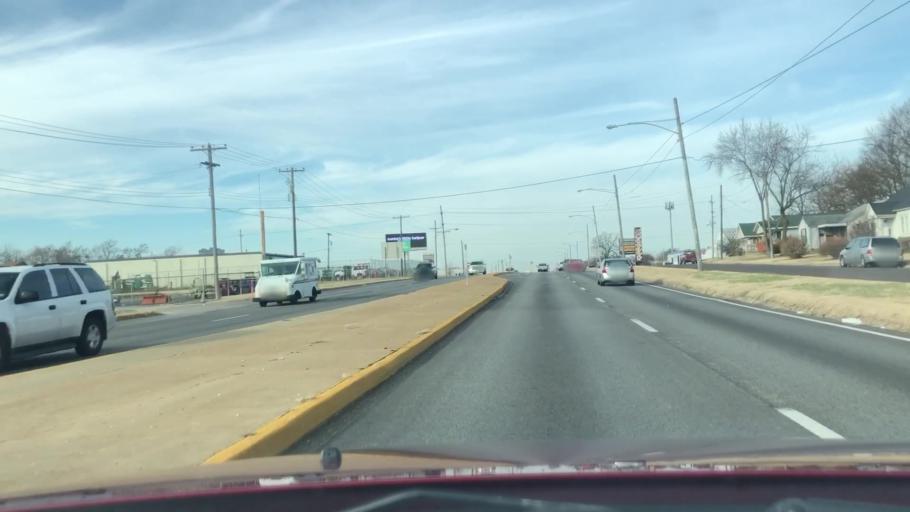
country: US
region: Missouri
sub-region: Greene County
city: Springfield
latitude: 37.2147
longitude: -93.2644
